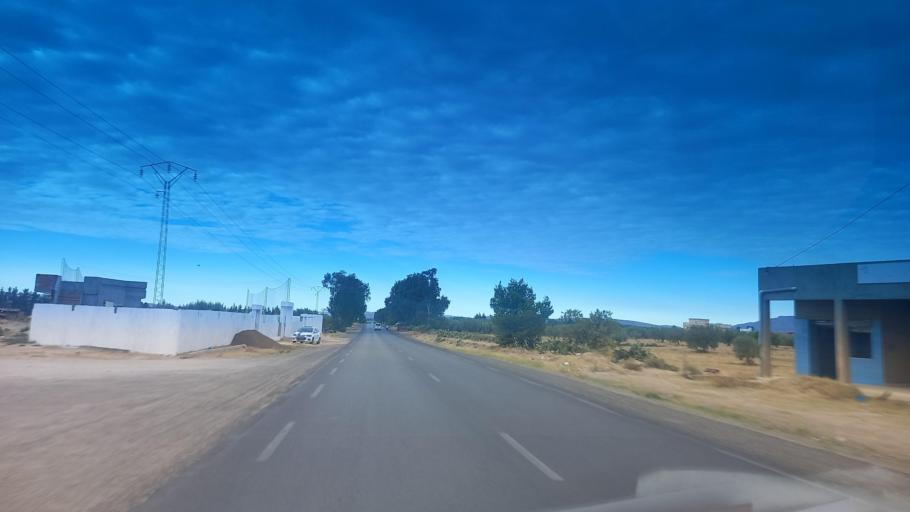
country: TN
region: Al Qasrayn
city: Sbiba
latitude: 35.2738
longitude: 9.0935
